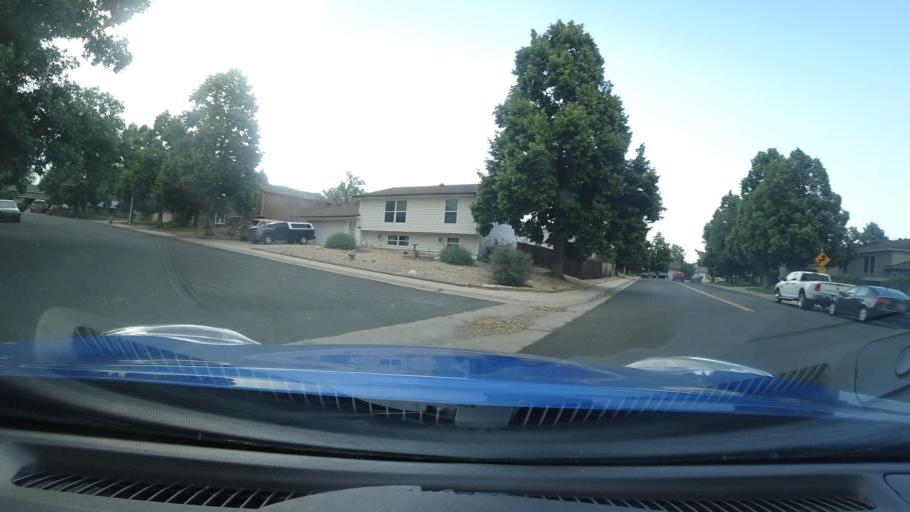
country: US
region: Colorado
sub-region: Adams County
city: Aurora
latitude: 39.6886
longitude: -104.8068
